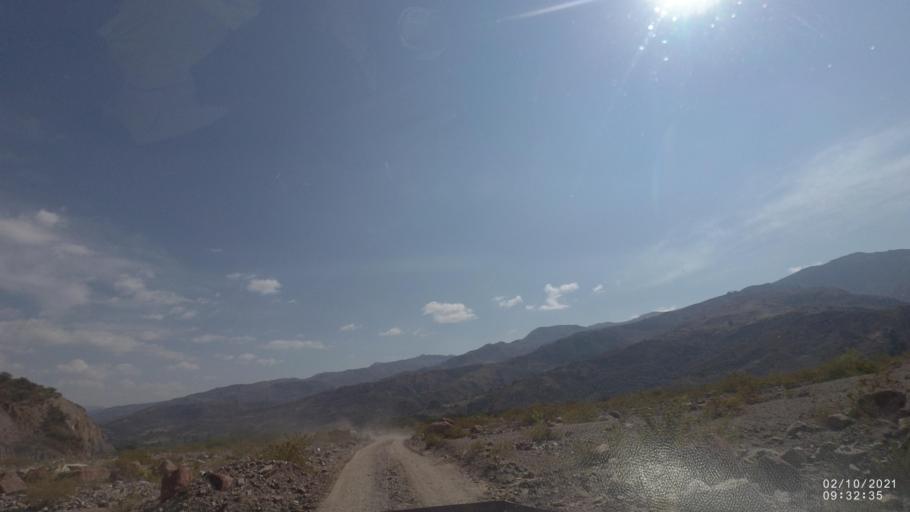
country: BO
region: Cochabamba
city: Irpa Irpa
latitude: -17.8458
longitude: -66.3204
